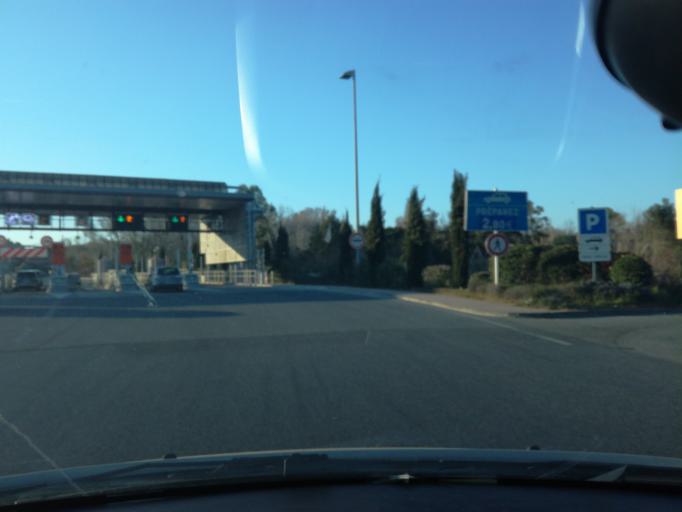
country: FR
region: Provence-Alpes-Cote d'Azur
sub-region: Departement du Var
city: Frejus
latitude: 43.4718
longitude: 6.7439
